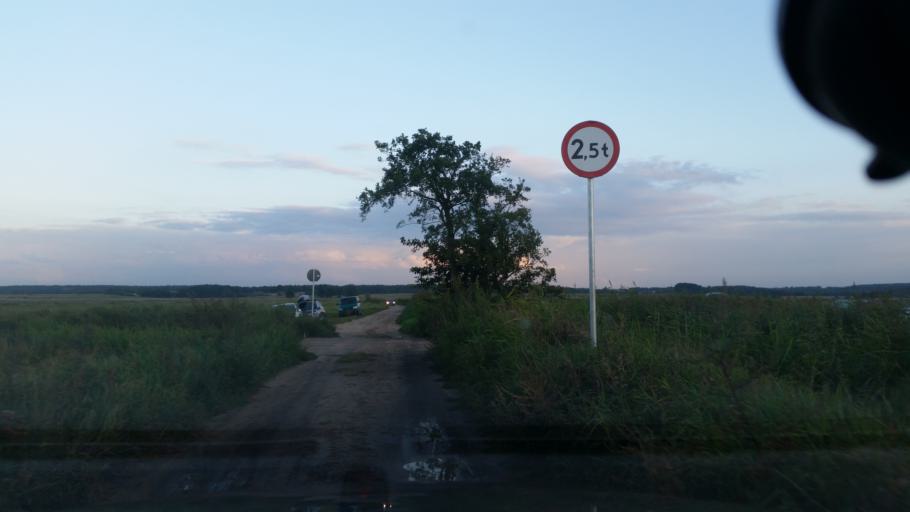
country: PL
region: Pomeranian Voivodeship
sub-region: Powiat wejherowski
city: Choczewo
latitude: 54.7896
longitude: 17.7933
